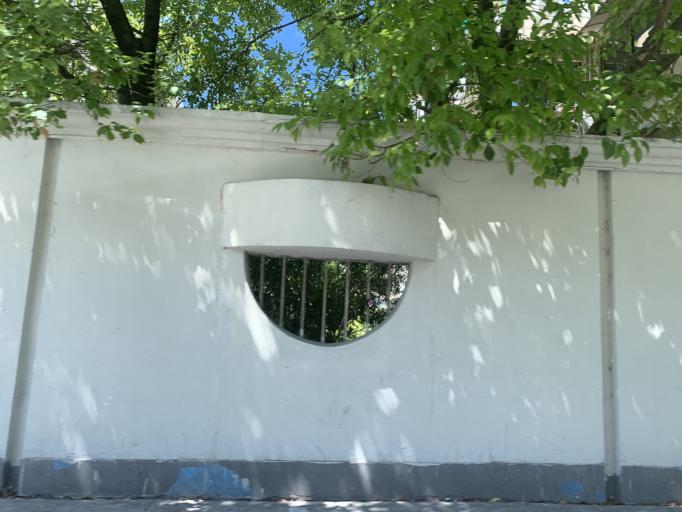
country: CN
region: Shanghai Shi
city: Huamu
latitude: 31.1748
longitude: 121.5354
